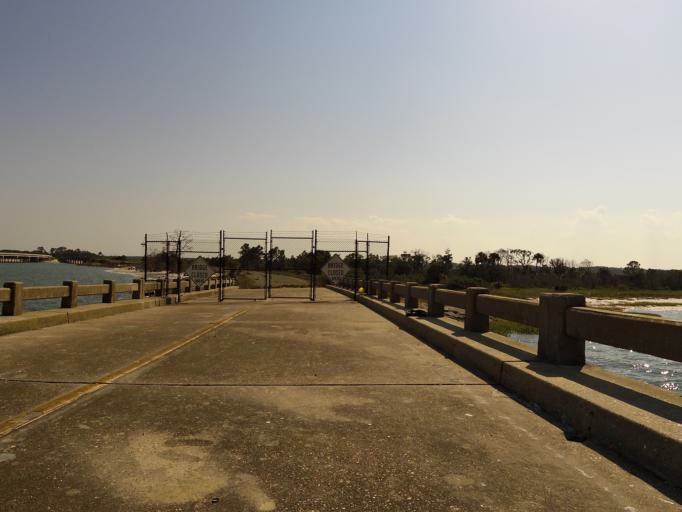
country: US
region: Florida
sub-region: Nassau County
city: Fernandina Beach
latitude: 30.5170
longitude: -81.4535
